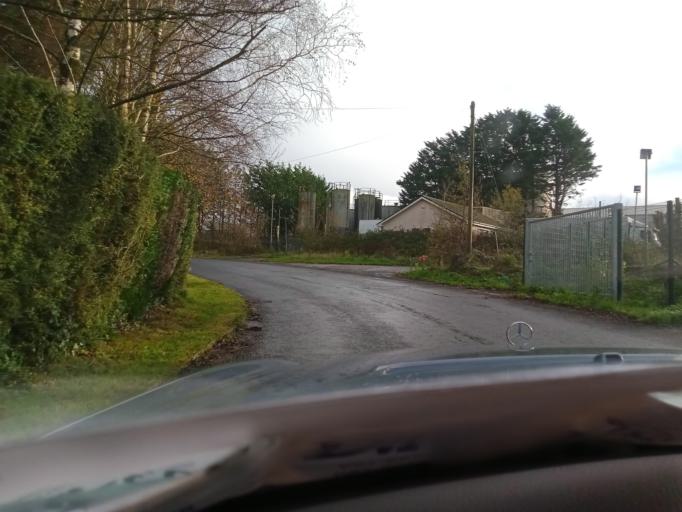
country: IE
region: Munster
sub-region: Waterford
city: Waterford
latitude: 52.2787
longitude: -7.1718
